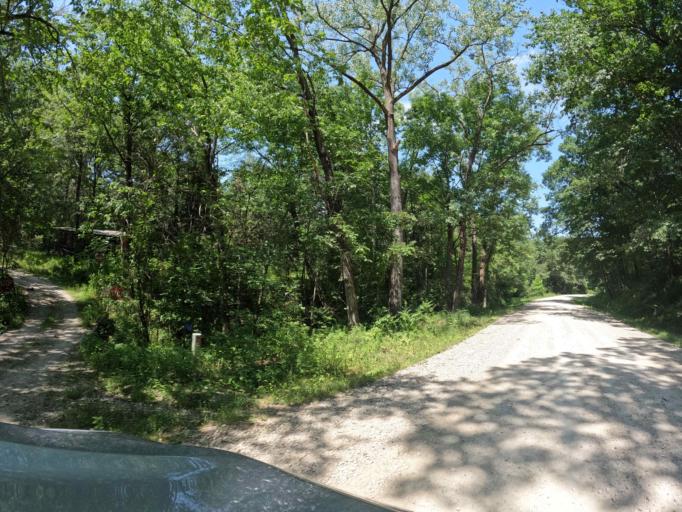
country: US
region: Iowa
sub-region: Henry County
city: Mount Pleasant
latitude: 40.8908
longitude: -91.6858
